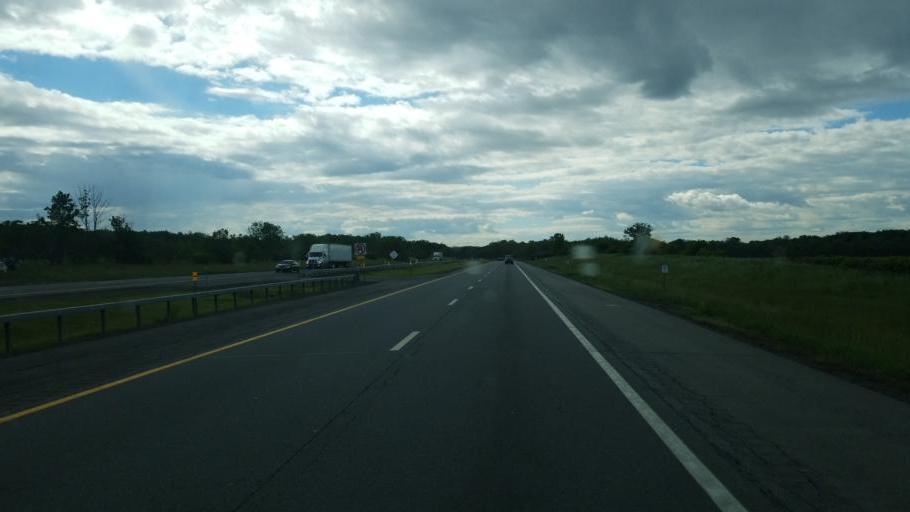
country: US
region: New York
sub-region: Ontario County
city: Phelps
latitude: 42.9615
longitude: -77.0410
